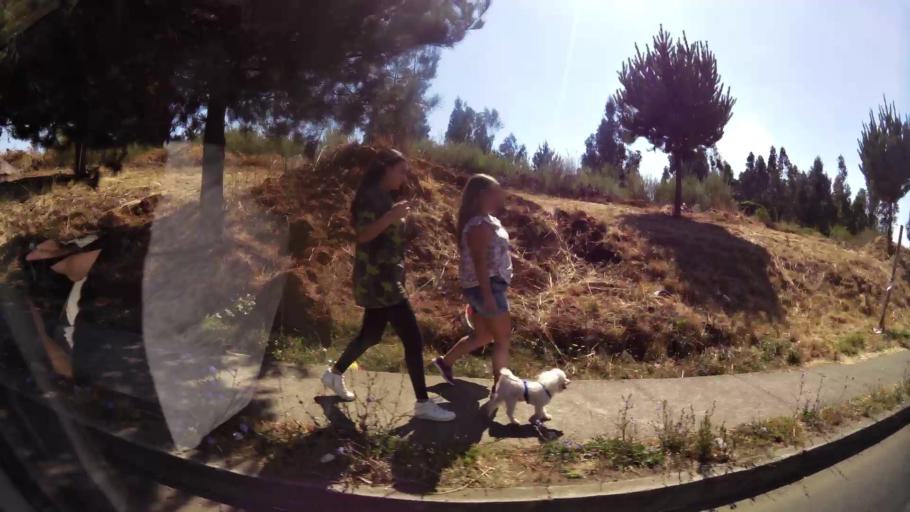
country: CL
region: Biobio
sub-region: Provincia de Concepcion
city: Concepcion
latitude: -36.7868
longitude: -73.0547
